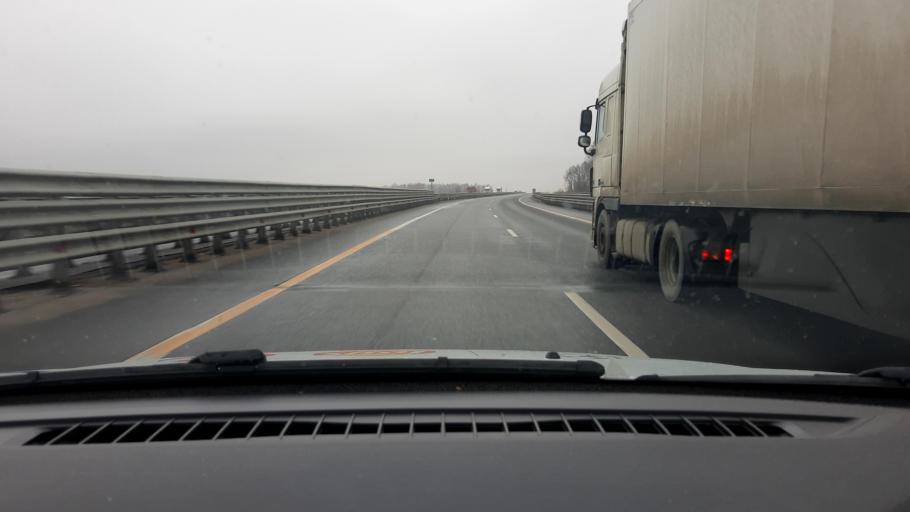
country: RU
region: Nizjnij Novgorod
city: Burevestnik
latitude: 56.1269
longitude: 43.7864
